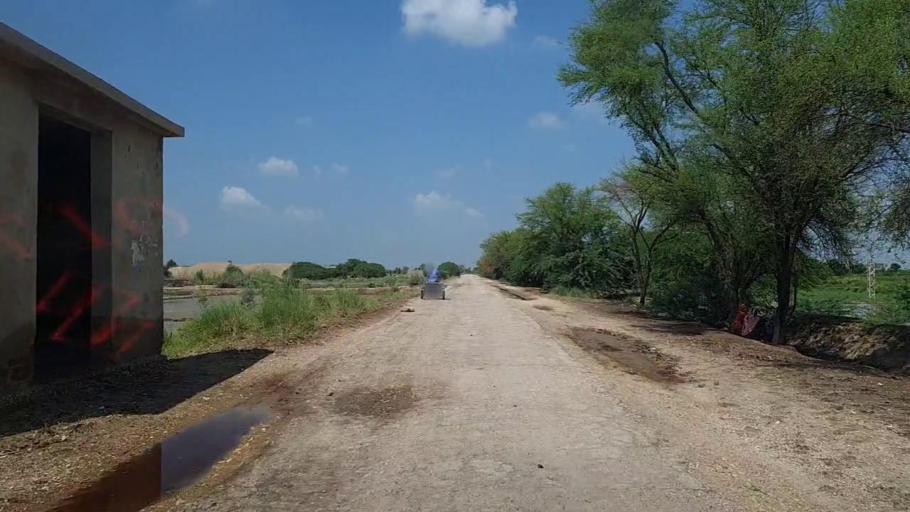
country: PK
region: Sindh
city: Kandiaro
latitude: 27.0097
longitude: 68.2625
